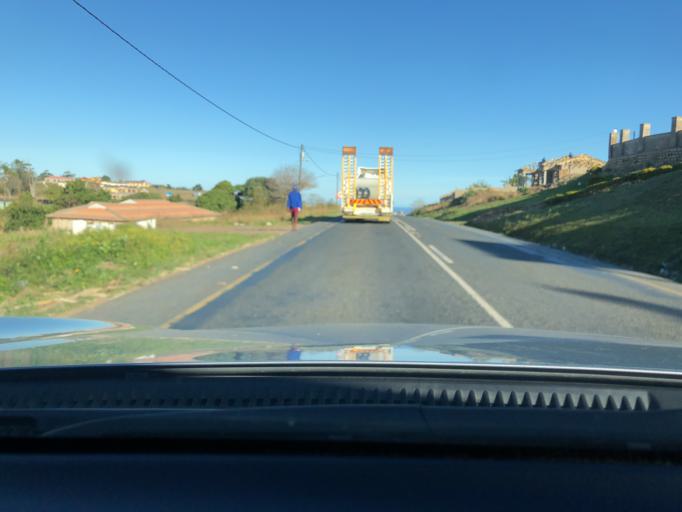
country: ZA
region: KwaZulu-Natal
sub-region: eThekwini Metropolitan Municipality
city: Umkomaas
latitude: -30.0036
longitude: 30.8015
